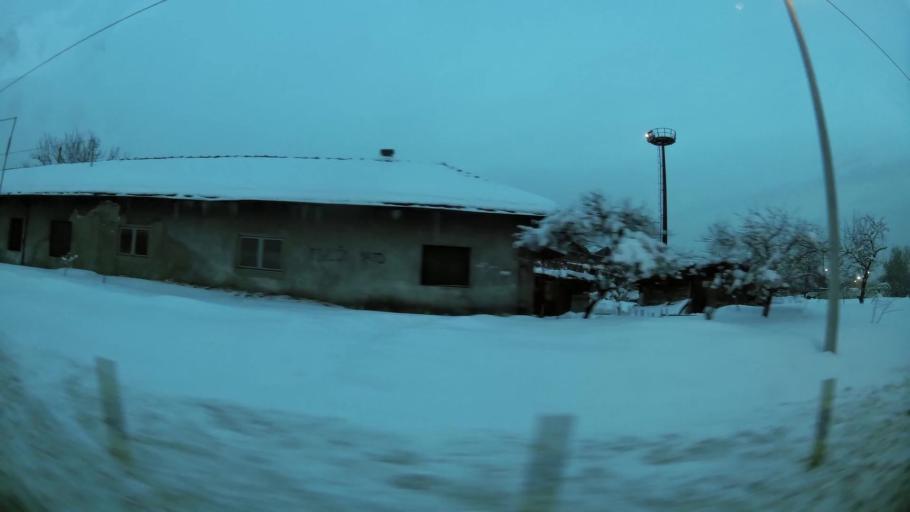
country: RS
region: Central Serbia
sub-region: Belgrade
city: Stari Grad
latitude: 44.8228
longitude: 20.4723
